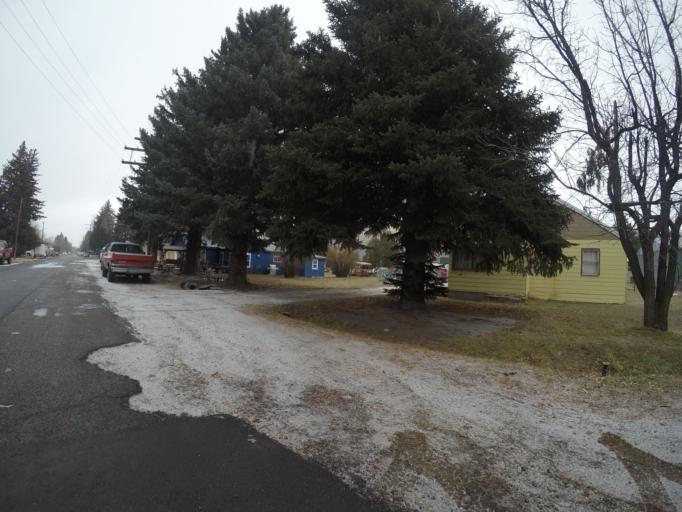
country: US
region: Montana
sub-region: Stillwater County
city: Absarokee
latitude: 45.5152
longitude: -109.4458
